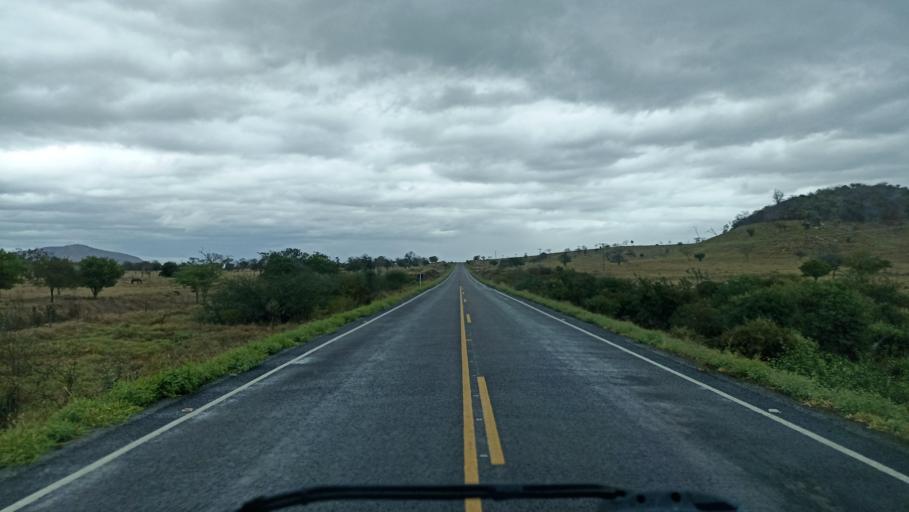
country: BR
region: Bahia
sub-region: Iacu
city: Iacu
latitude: -12.9640
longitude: -40.4853
